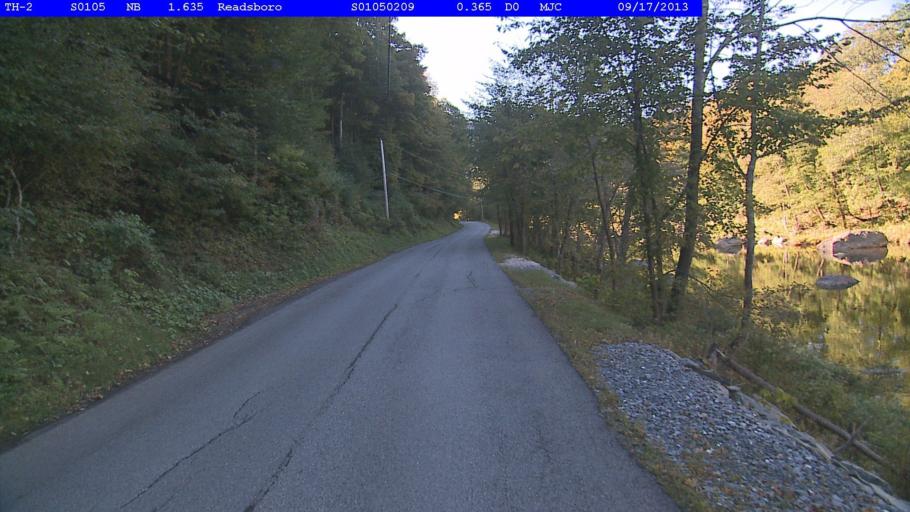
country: US
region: Massachusetts
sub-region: Franklin County
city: Charlemont
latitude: 42.7587
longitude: -72.9355
